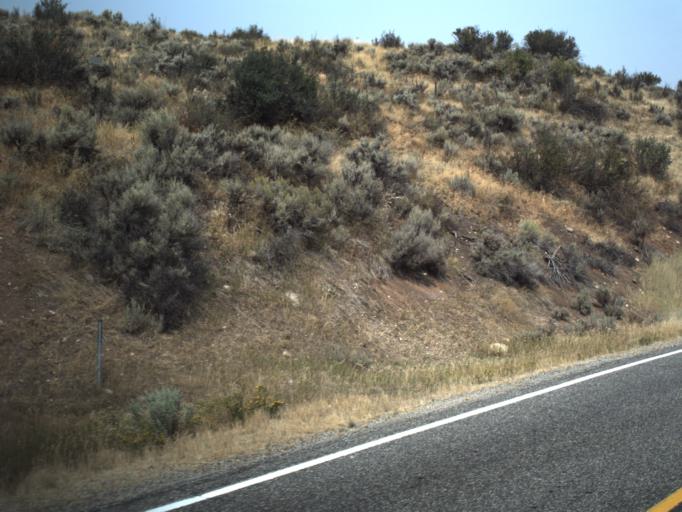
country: US
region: Utah
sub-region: Morgan County
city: Morgan
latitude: 40.9833
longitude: -111.5387
